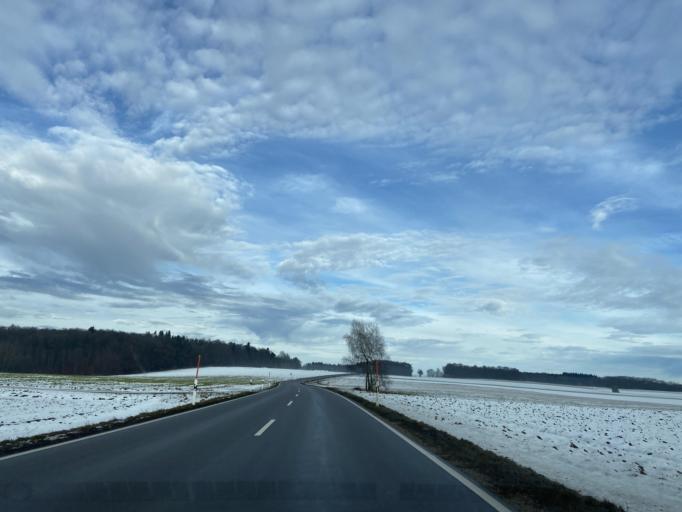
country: DE
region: Baden-Wuerttemberg
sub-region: Tuebingen Region
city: Hettingen
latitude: 48.2007
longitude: 9.2828
